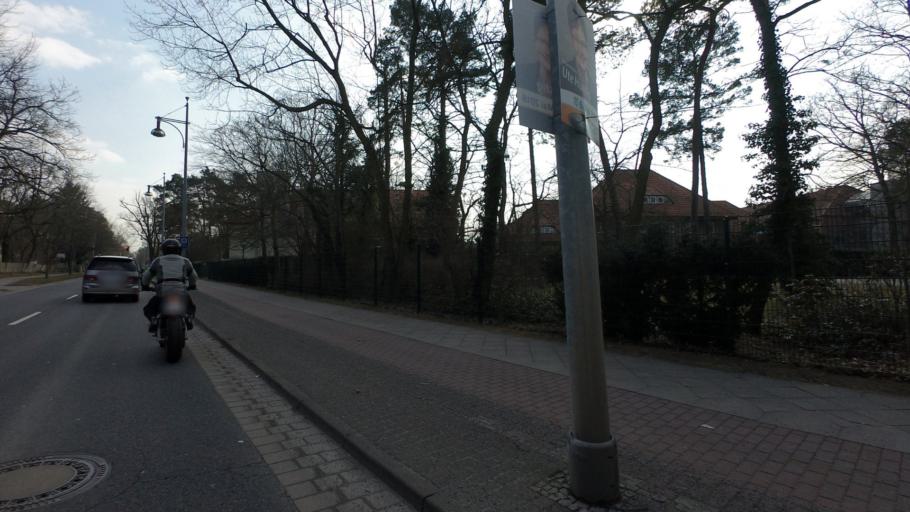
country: DE
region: Brandenburg
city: Potsdam
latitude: 52.3431
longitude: 13.1079
